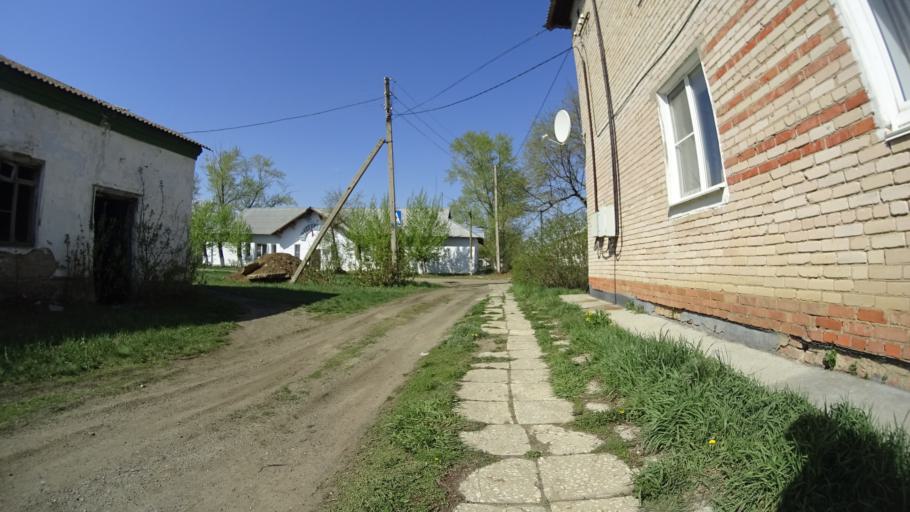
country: RU
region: Chelyabinsk
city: Troitsk
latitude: 54.1900
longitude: 61.5065
